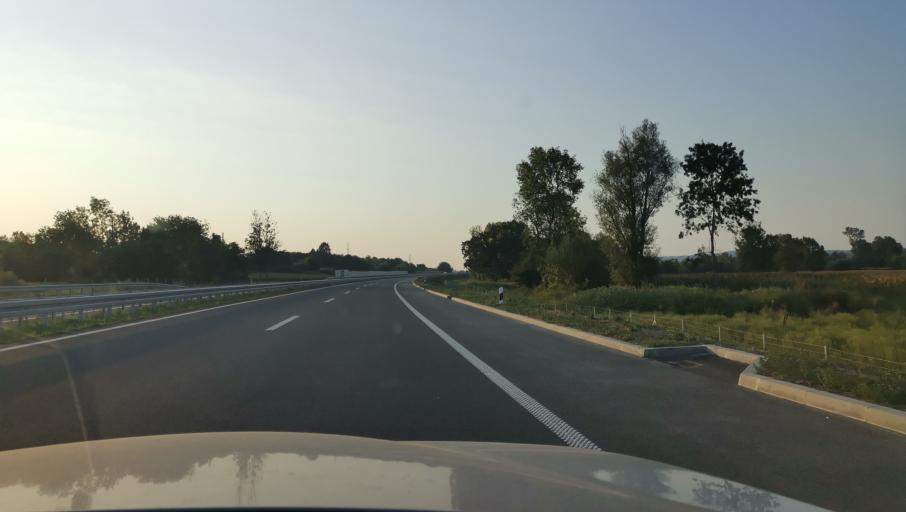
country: RS
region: Central Serbia
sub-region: Kolubarski Okrug
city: Ljig
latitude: 44.2917
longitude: 20.2395
